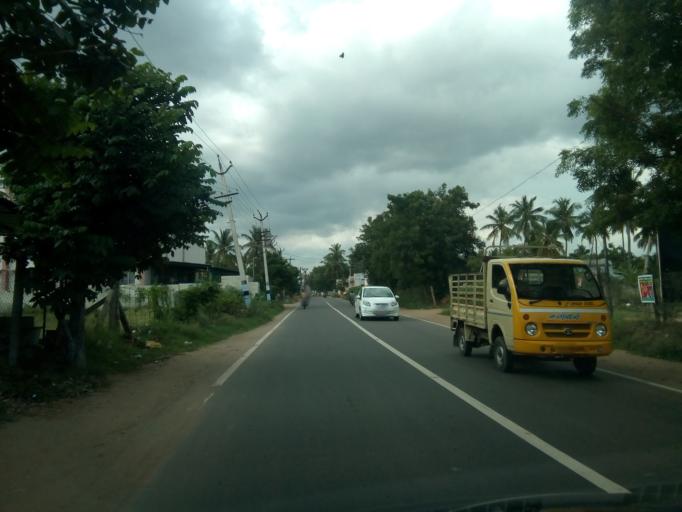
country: IN
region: Tamil Nadu
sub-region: Coimbatore
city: Irugur
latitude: 11.0819
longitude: 77.0351
